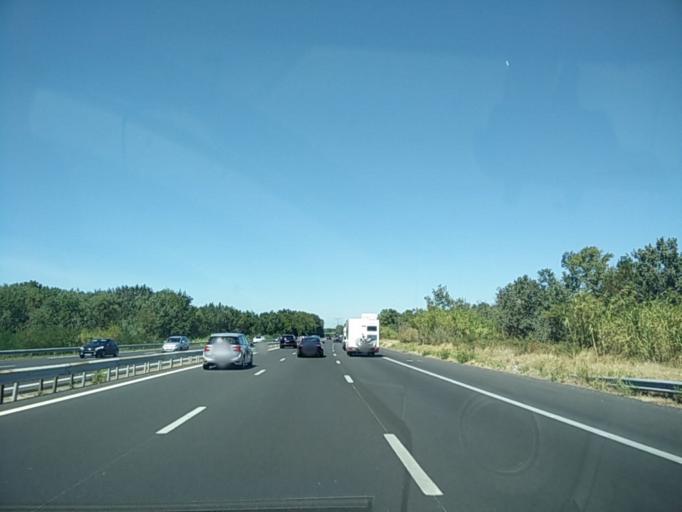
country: FR
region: Provence-Alpes-Cote d'Azur
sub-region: Departement des Bouches-du-Rhone
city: Cabannes
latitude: 43.8583
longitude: 4.9778
